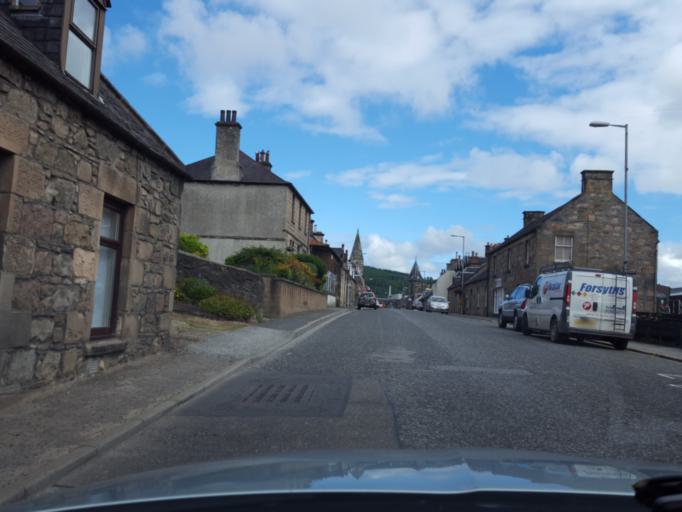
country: GB
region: Scotland
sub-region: Moray
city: Rothes
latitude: 57.5248
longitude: -3.2083
